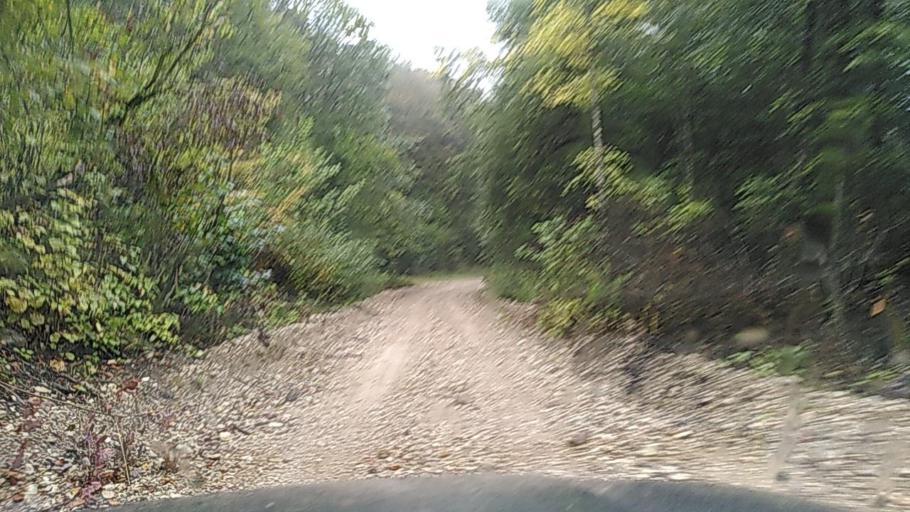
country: RU
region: Kabardino-Balkariya
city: Belaya Rechka
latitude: 43.3831
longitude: 43.4360
